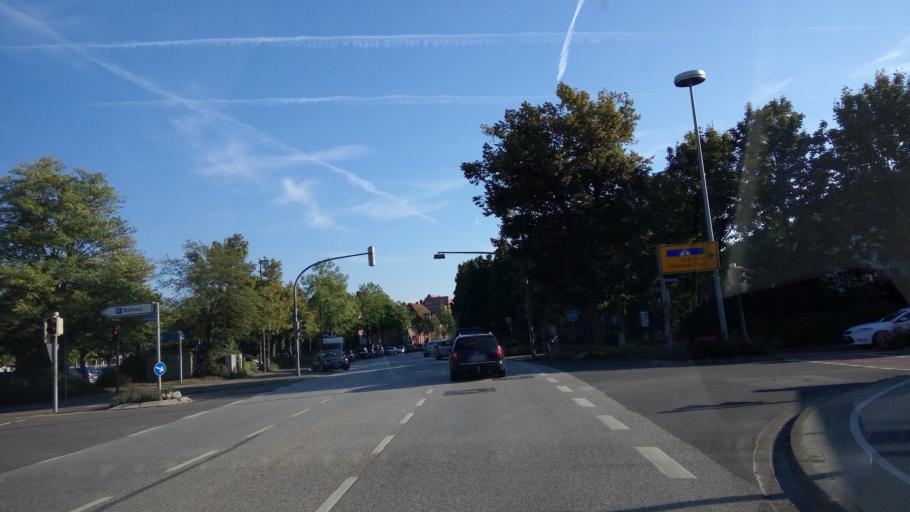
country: DE
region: Schleswig-Holstein
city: Eckernforde
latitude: 54.4712
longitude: 9.8345
